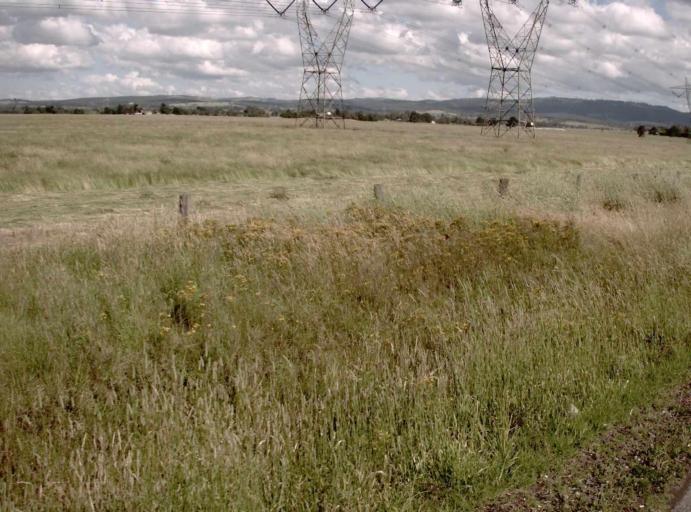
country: AU
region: Victoria
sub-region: Latrobe
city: Morwell
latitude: -38.2580
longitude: 146.4342
